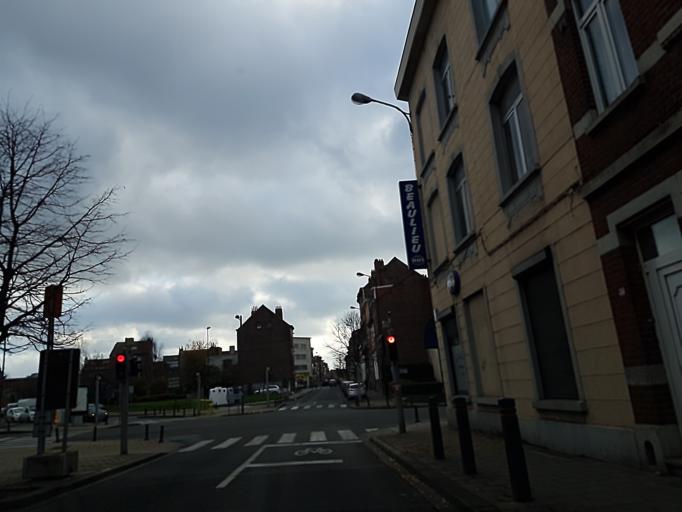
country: BE
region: Flanders
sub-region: Provincie Vlaams-Brabant
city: Diegem
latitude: 50.8719
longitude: 4.3947
